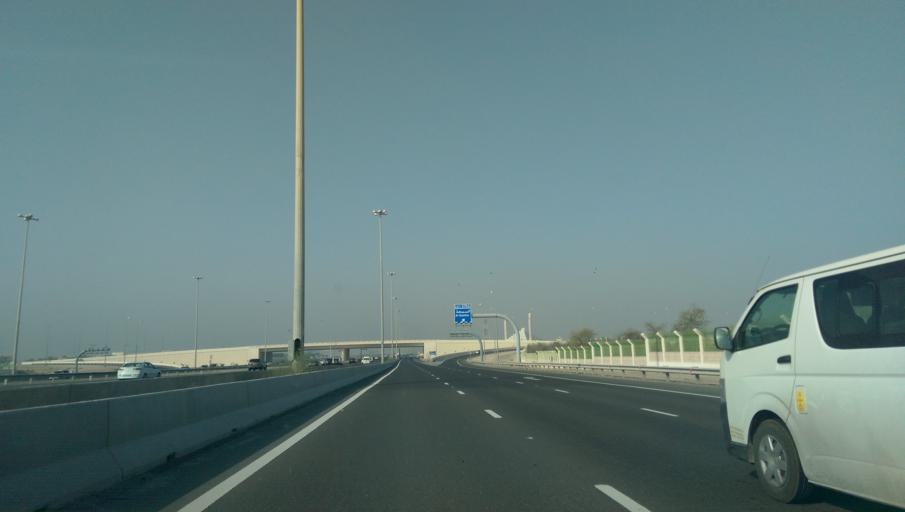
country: AE
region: Abu Dhabi
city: Abu Dhabi
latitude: 24.6892
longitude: 54.7749
